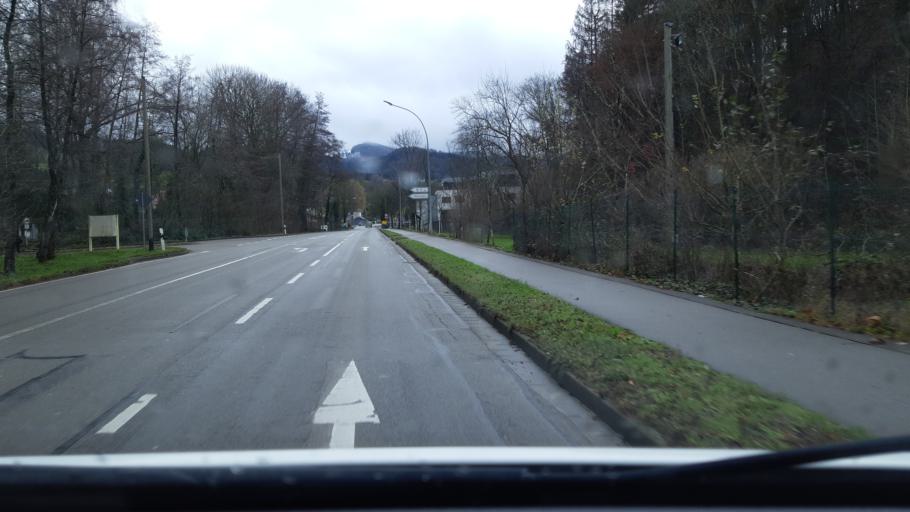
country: DE
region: Baden-Wuerttemberg
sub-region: Freiburg Region
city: Merzhausen
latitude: 47.9617
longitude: 7.8306
